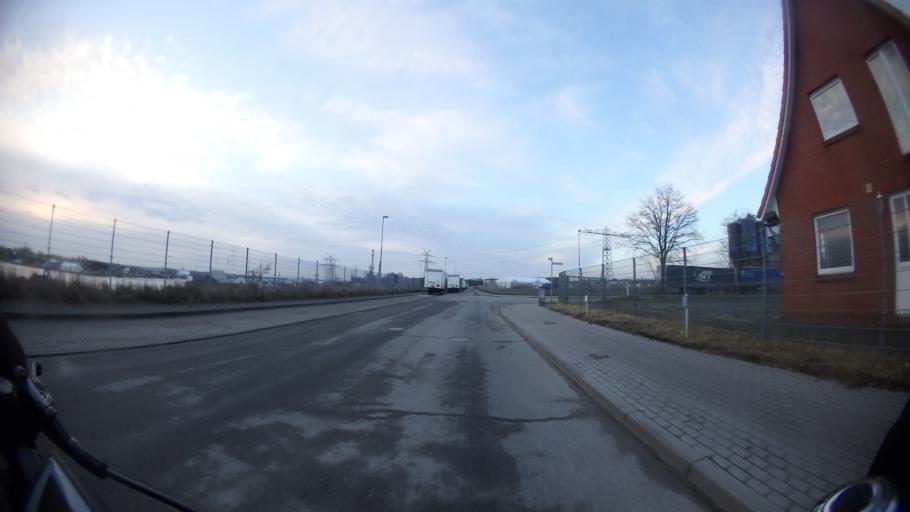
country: DE
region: Mecklenburg-Vorpommern
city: Selmsdorf
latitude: 53.8967
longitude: 10.8101
